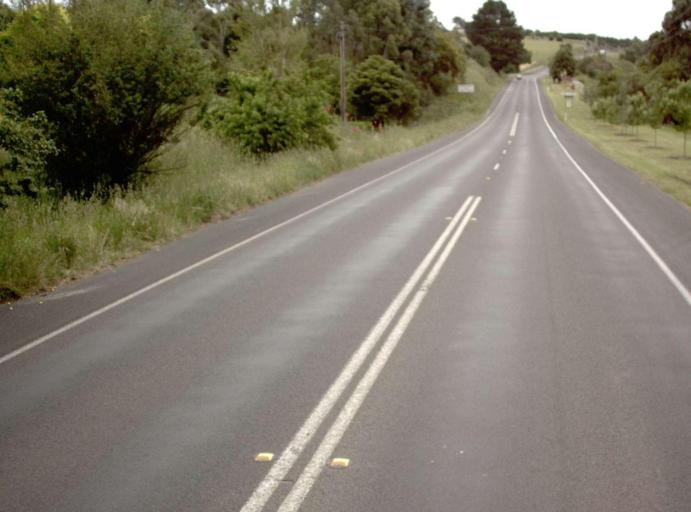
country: AU
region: Victoria
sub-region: Baw Baw
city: Warragul
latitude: -38.4700
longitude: 145.9401
